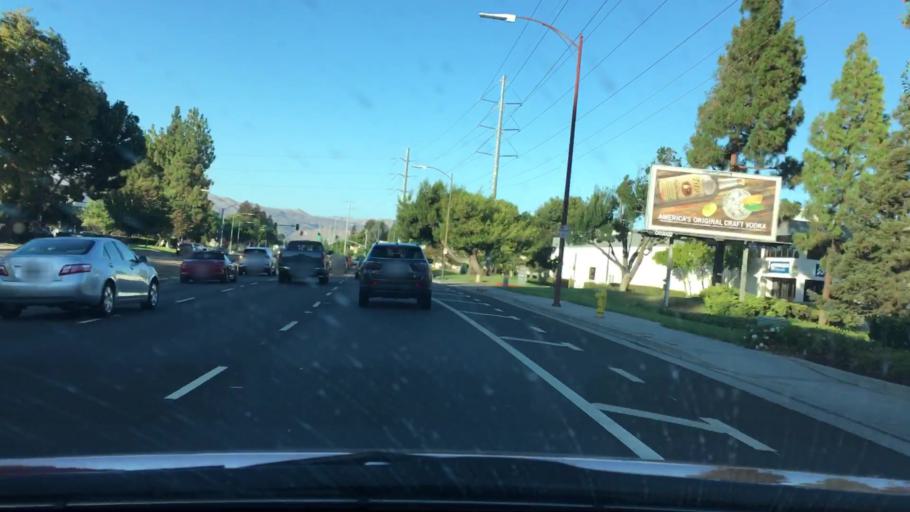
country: US
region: California
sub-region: Santa Clara County
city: Santa Clara
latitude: 37.3868
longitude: -121.9259
